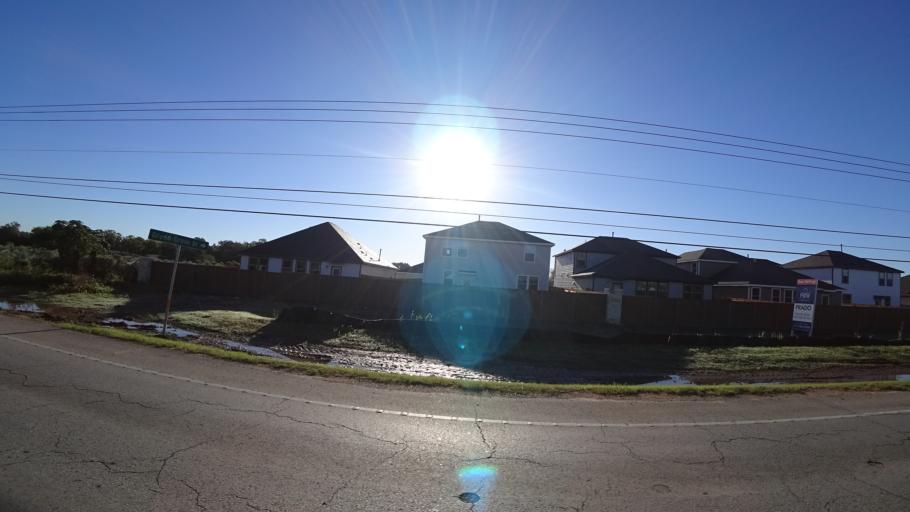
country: US
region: Texas
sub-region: Travis County
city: Hornsby Bend
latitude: 30.2211
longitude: -97.6345
